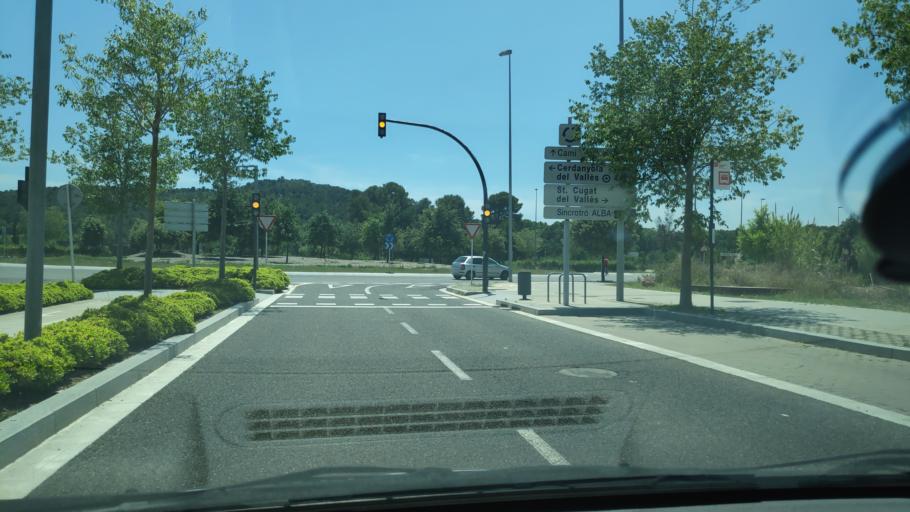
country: ES
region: Catalonia
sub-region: Provincia de Barcelona
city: Cerdanyola del Valles
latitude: 41.4860
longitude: 2.1147
